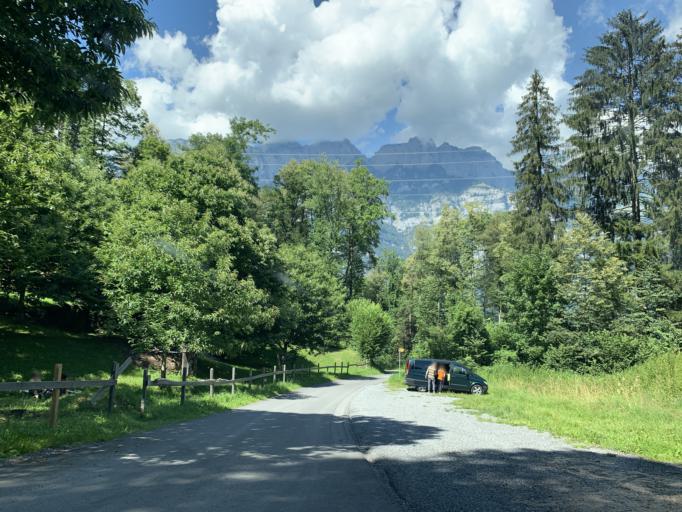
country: CH
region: Saint Gallen
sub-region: Wahlkreis Sarganserland
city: Quarten
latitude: 47.1055
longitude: 9.2127
